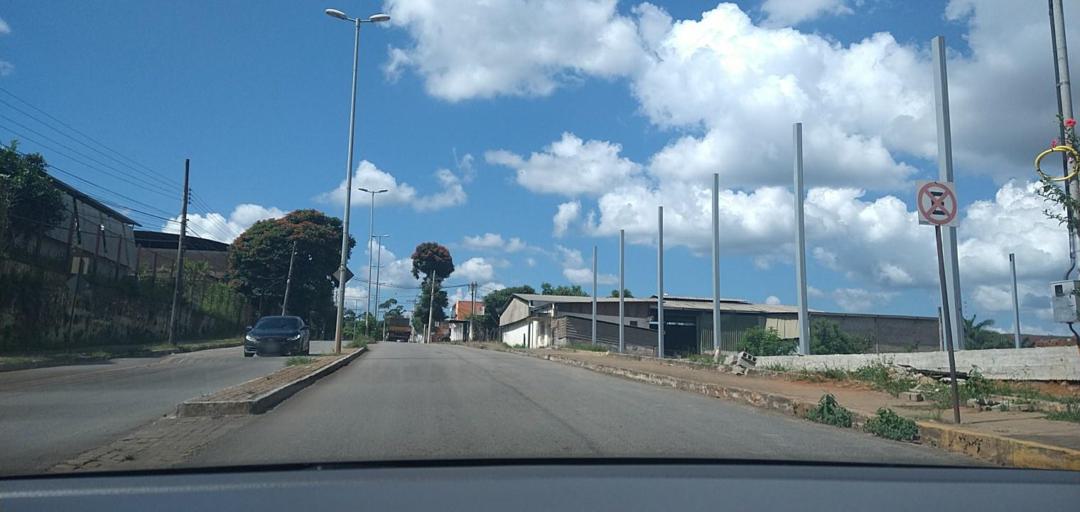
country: BR
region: Minas Gerais
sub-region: Joao Monlevade
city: Joao Monlevade
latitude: -19.8328
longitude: -43.1888
